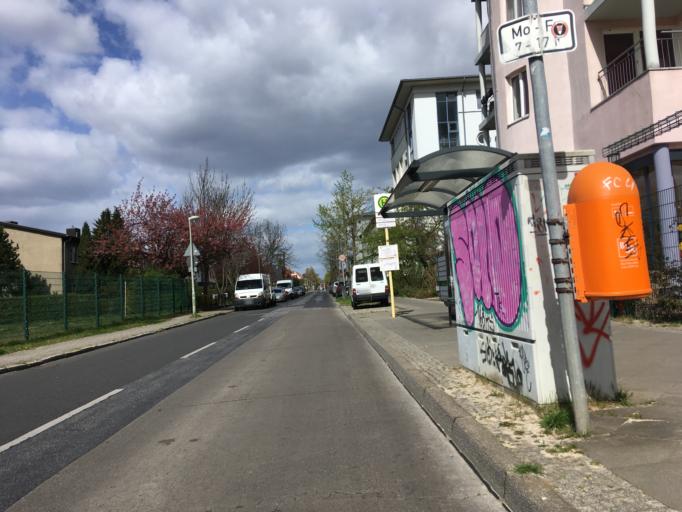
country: DE
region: Berlin
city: Altglienicke
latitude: 52.4094
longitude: 13.5347
